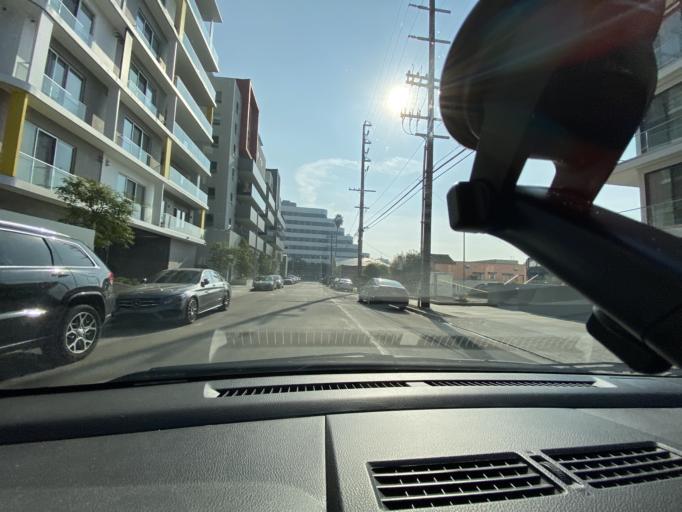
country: US
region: California
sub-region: Los Angeles County
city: Culver City
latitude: 34.0221
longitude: -118.3988
